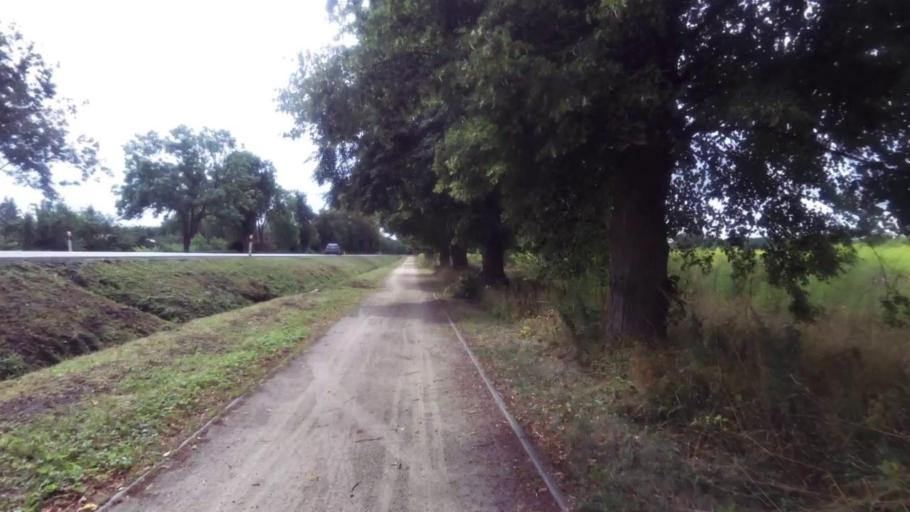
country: PL
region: West Pomeranian Voivodeship
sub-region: Powiat mysliborski
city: Debno
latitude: 52.7283
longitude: 14.6938
